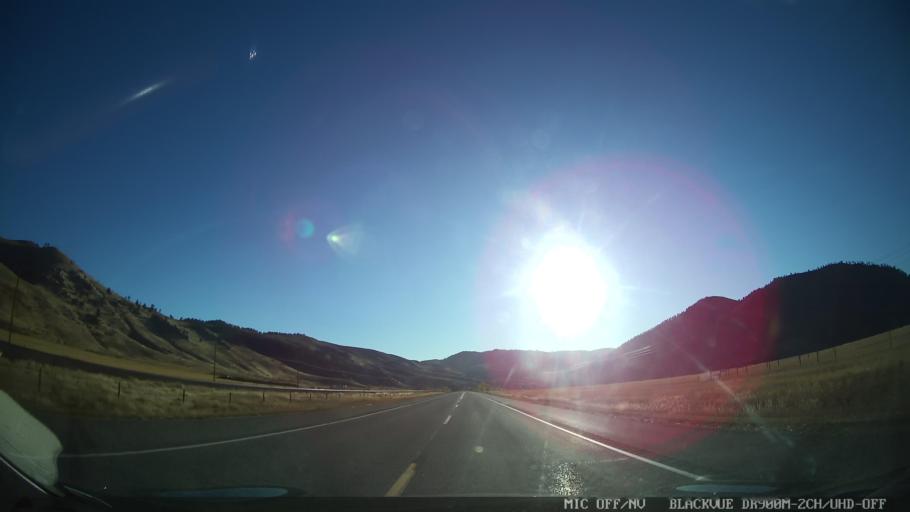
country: US
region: Colorado
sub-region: Grand County
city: Hot Sulphur Springs
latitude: 40.0512
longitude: -106.1463
